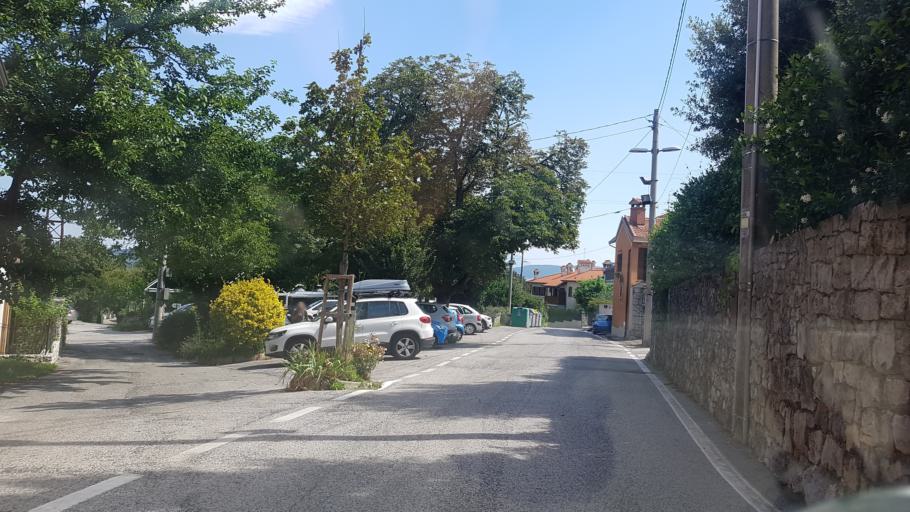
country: IT
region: Friuli Venezia Giulia
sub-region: Provincia di Trieste
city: Villa Opicina
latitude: 45.6782
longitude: 13.8028
